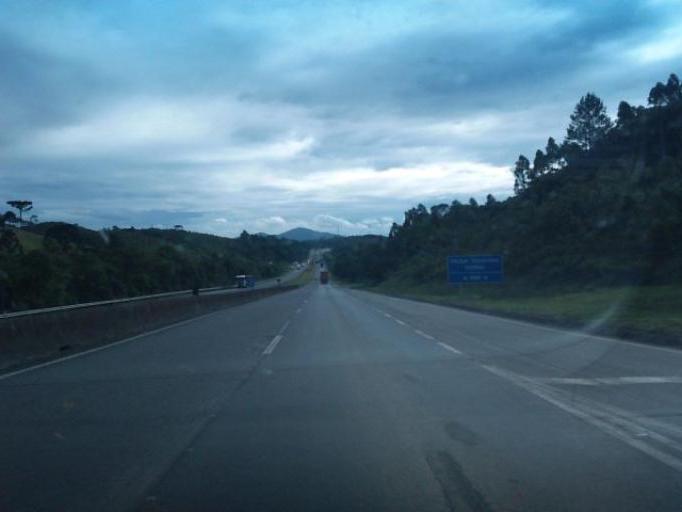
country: BR
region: Parana
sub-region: Campina Grande Do Sul
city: Campina Grande do Sul
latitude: -25.2747
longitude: -48.9227
